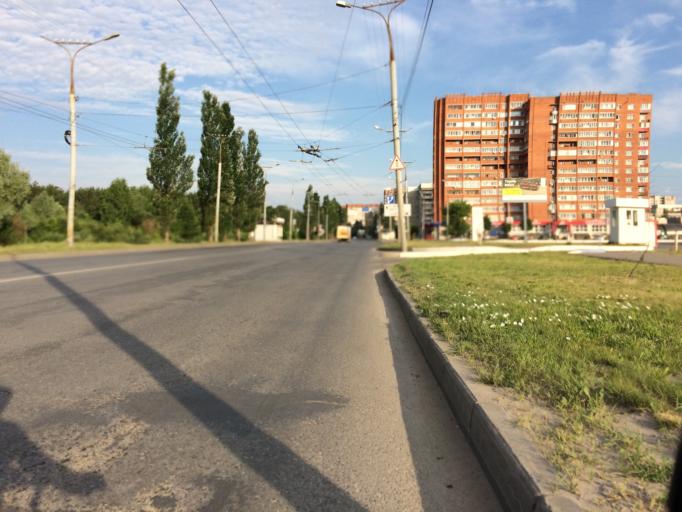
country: RU
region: Mariy-El
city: Yoshkar-Ola
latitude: 56.6248
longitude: 47.9277
